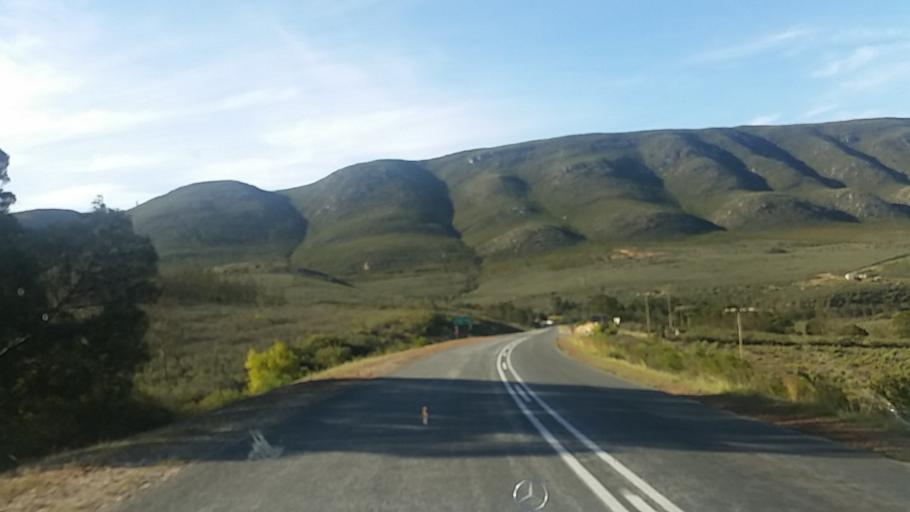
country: ZA
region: Western Cape
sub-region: Eden District Municipality
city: Knysna
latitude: -33.7676
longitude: 22.9618
